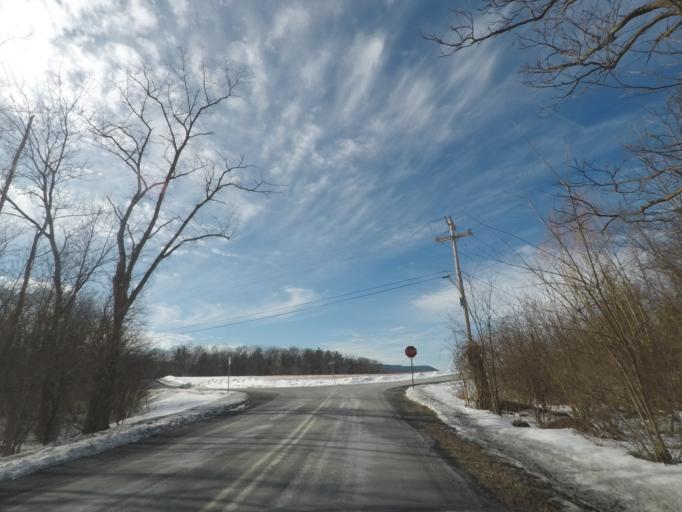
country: US
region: New York
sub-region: Albany County
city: Voorheesville
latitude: 42.6593
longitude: -73.9637
